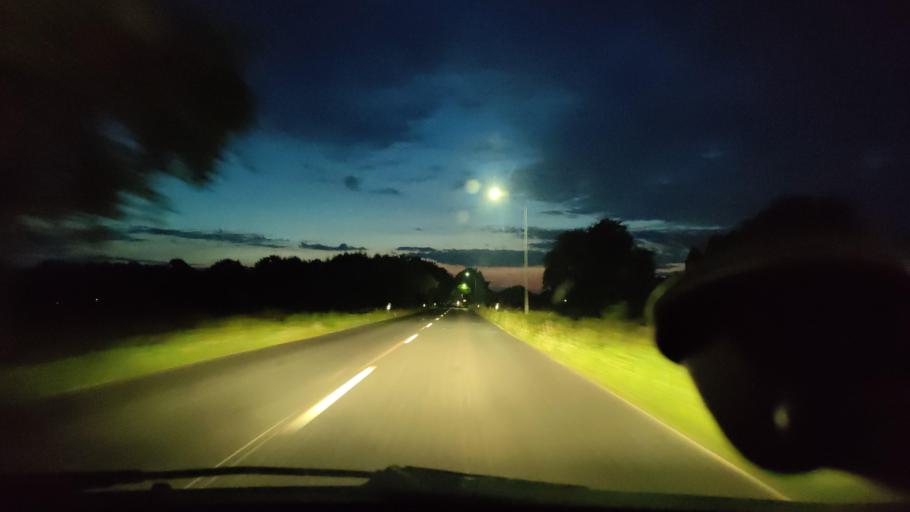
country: DE
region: North Rhine-Westphalia
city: Rheinberg
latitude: 51.5853
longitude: 6.5685
